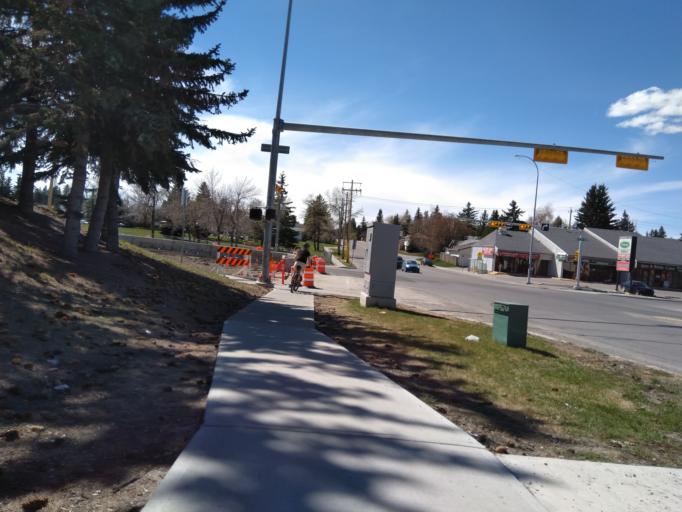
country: CA
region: Alberta
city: Calgary
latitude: 51.0124
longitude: -114.1406
